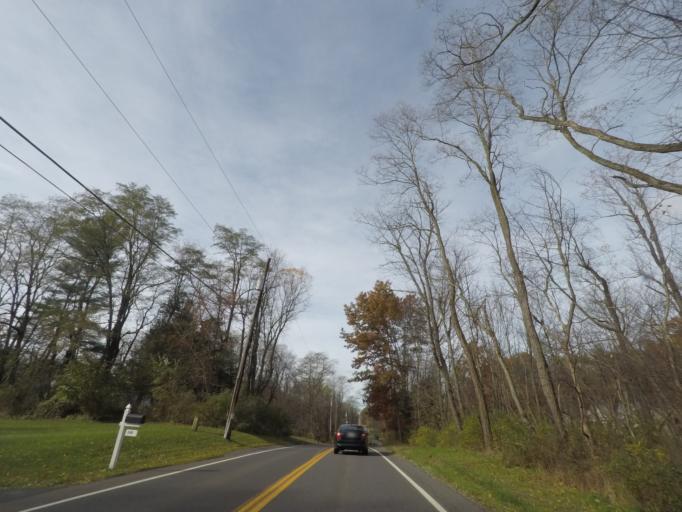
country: US
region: New York
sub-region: Albany County
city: Westmere
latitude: 42.7340
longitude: -73.9084
